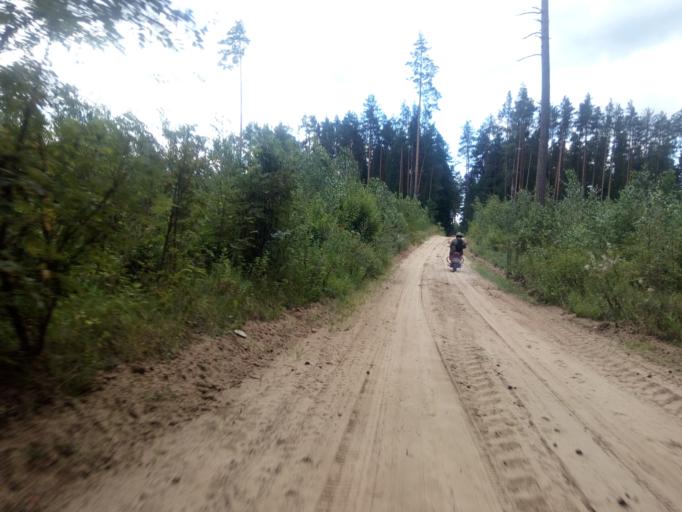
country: BY
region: Vitebsk
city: Dzisna
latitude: 55.6984
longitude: 28.3540
